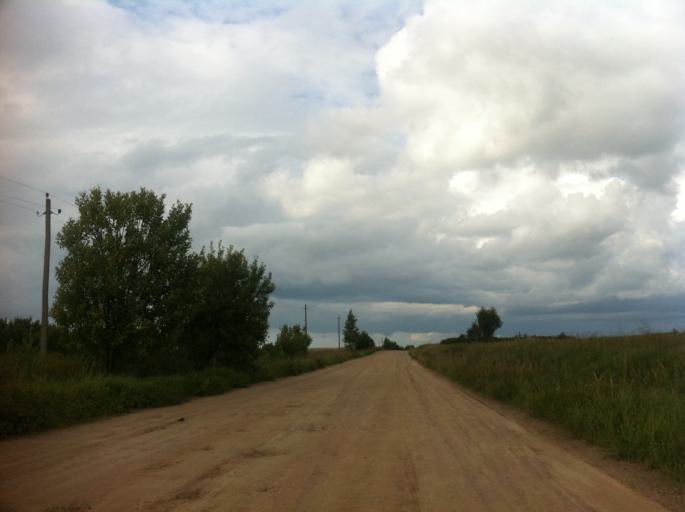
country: RU
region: Pskov
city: Izborsk
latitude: 57.8207
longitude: 27.9781
